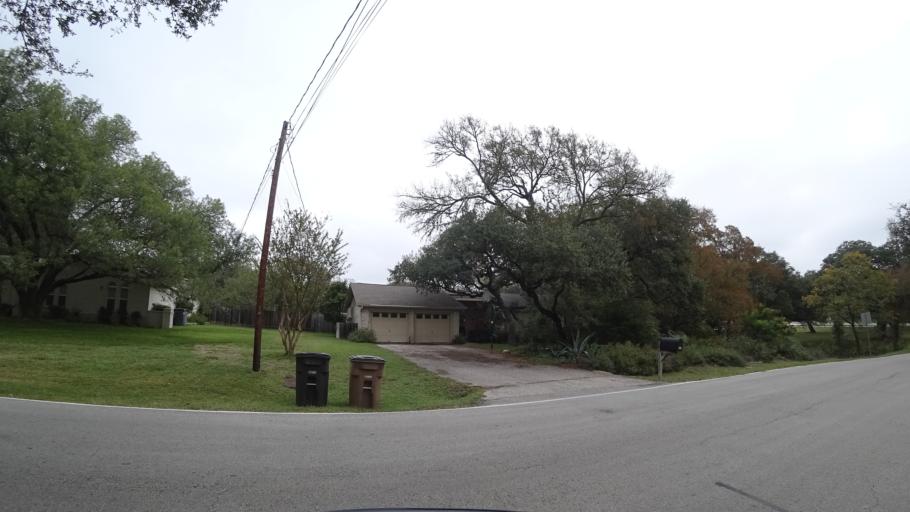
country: US
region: Texas
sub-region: Travis County
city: Barton Creek
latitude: 30.2231
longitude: -97.9016
